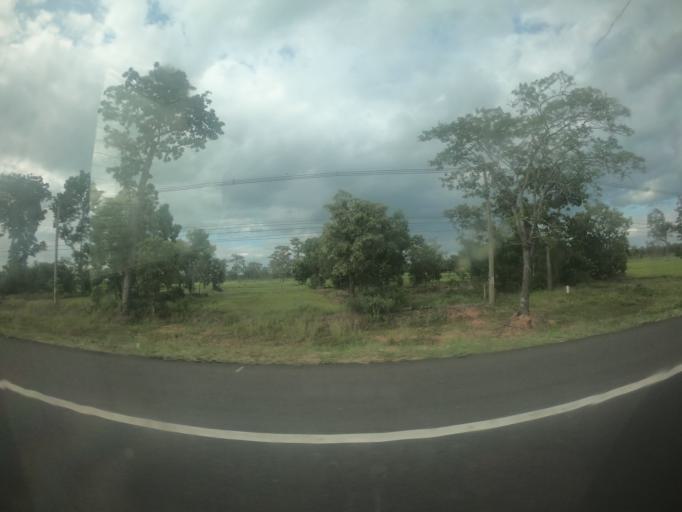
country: TH
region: Surin
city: Kap Choeng
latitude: 14.5206
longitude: 103.5418
